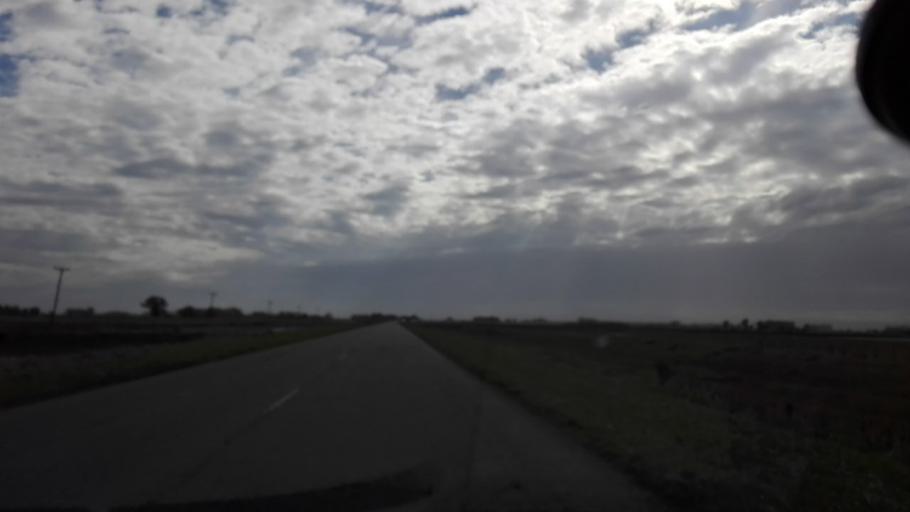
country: AR
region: Buenos Aires
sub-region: Partido de Las Flores
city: Las Flores
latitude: -36.0857
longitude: -59.0896
